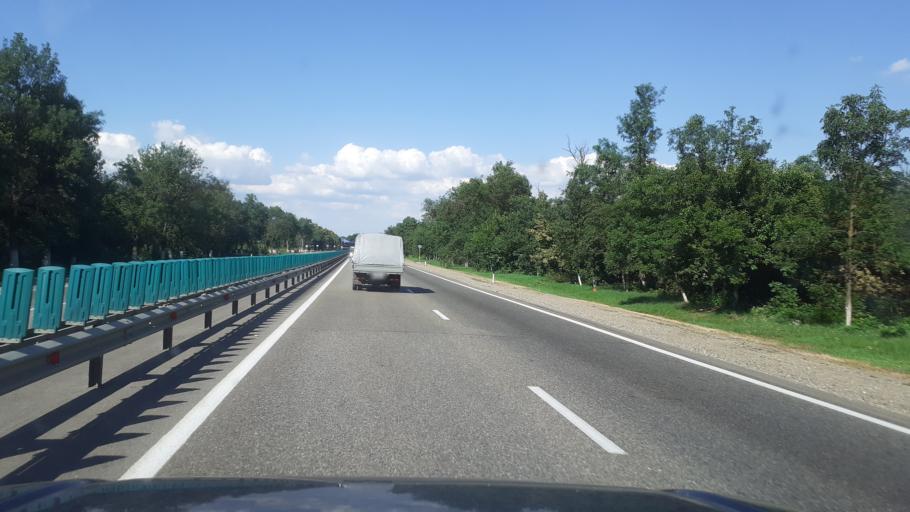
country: RU
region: Krasnodarskiy
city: Afipskiy
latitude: 44.8756
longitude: 38.7628
